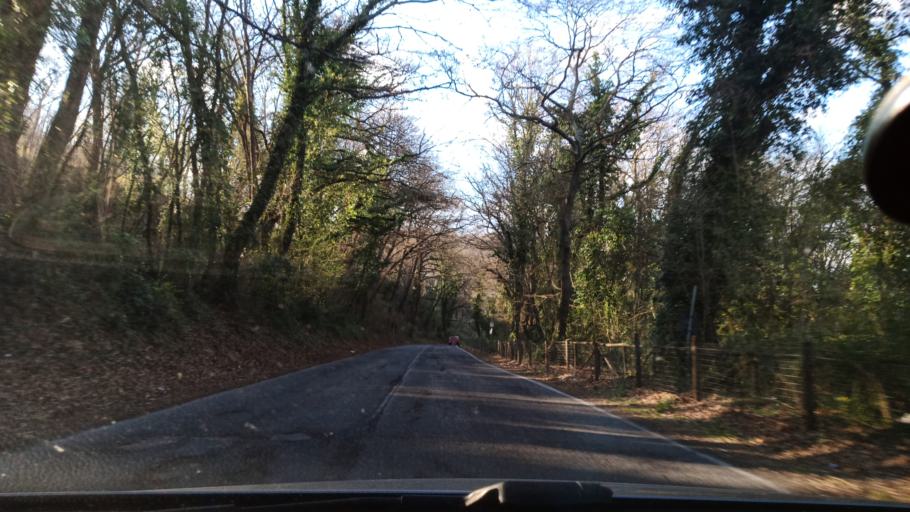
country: IT
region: Latium
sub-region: Citta metropolitana di Roma Capitale
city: Nazzano
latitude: 42.2078
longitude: 12.6045
